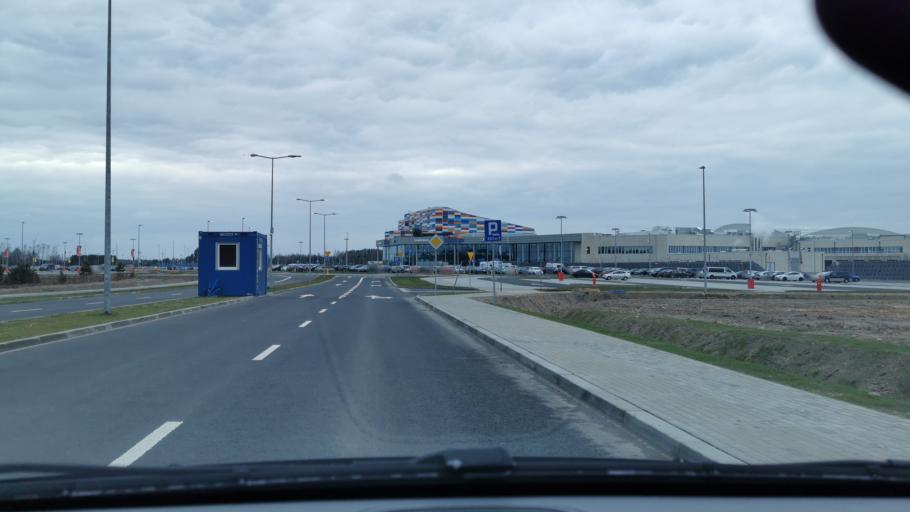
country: PL
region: Masovian Voivodeship
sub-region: Powiat zyrardowski
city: Mszczonow
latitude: 51.9899
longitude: 20.4625
